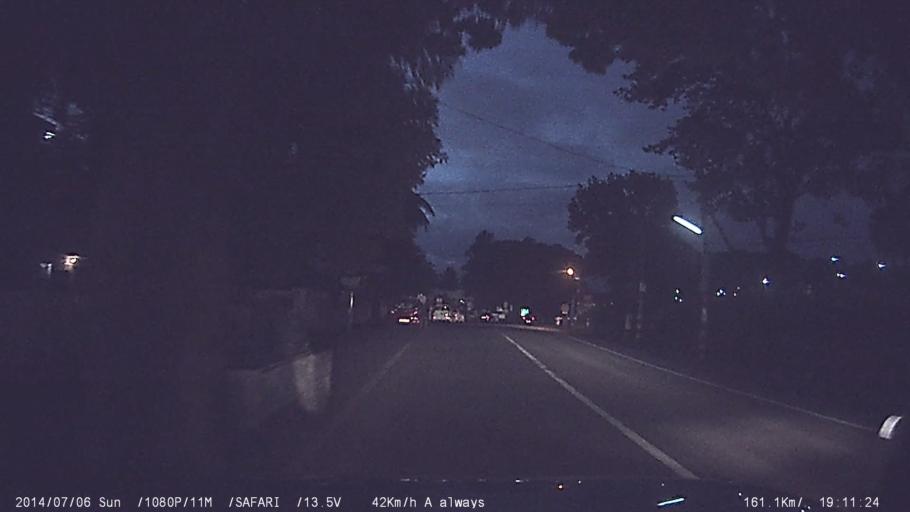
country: IN
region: Kerala
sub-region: Palakkad district
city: Palakkad
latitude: 10.7632
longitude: 76.6549
